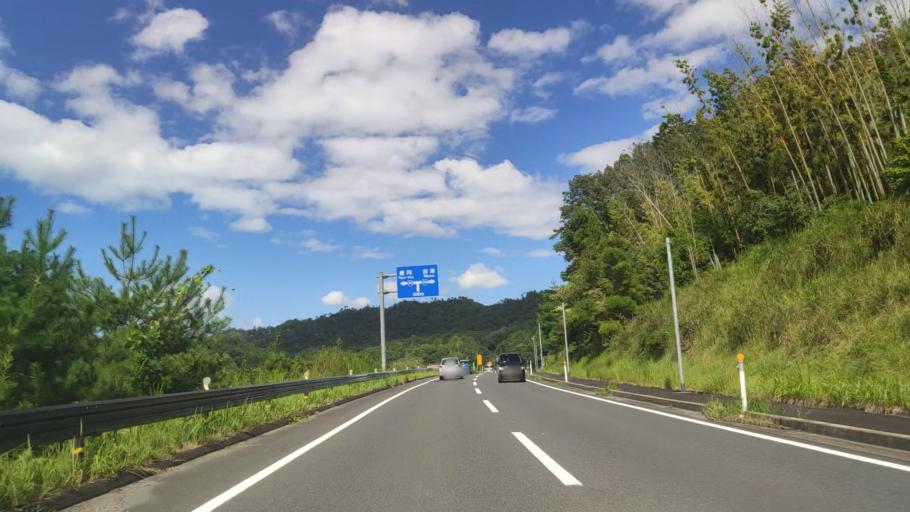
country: JP
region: Hyogo
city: Toyooka
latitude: 35.5709
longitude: 134.9763
